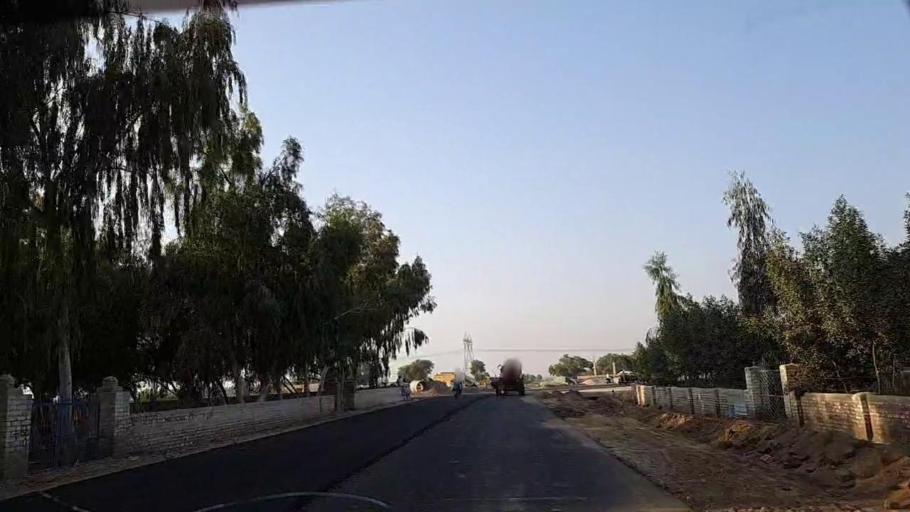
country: PK
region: Sindh
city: Rustam jo Goth
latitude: 27.9656
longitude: 68.8001
